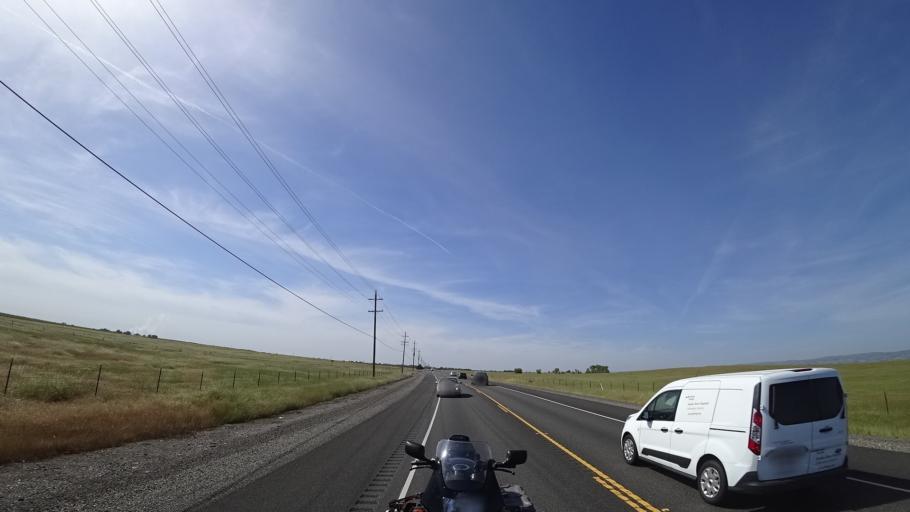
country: US
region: California
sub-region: Glenn County
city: Hamilton City
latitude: 39.8589
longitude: -121.9555
